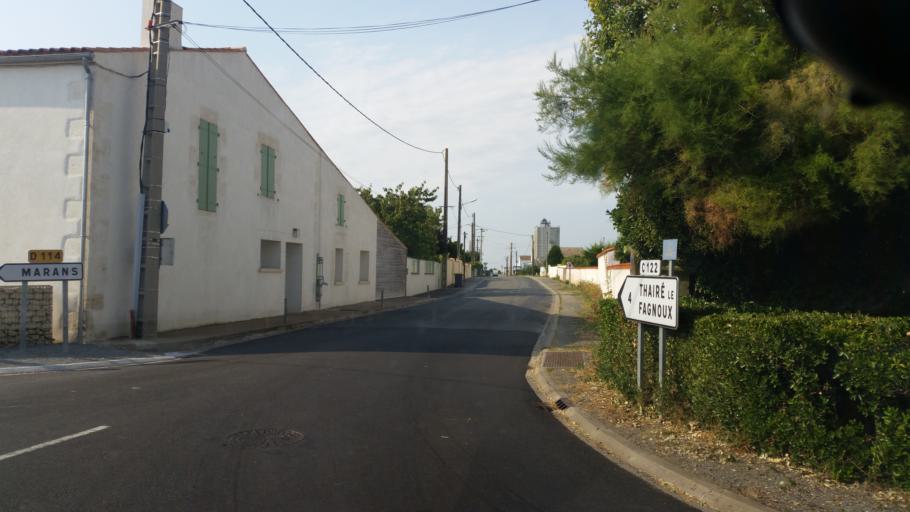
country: FR
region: Poitou-Charentes
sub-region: Departement de la Charente-Maritime
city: Saint-Jean-de-Liversay
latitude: 46.2680
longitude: -0.8820
